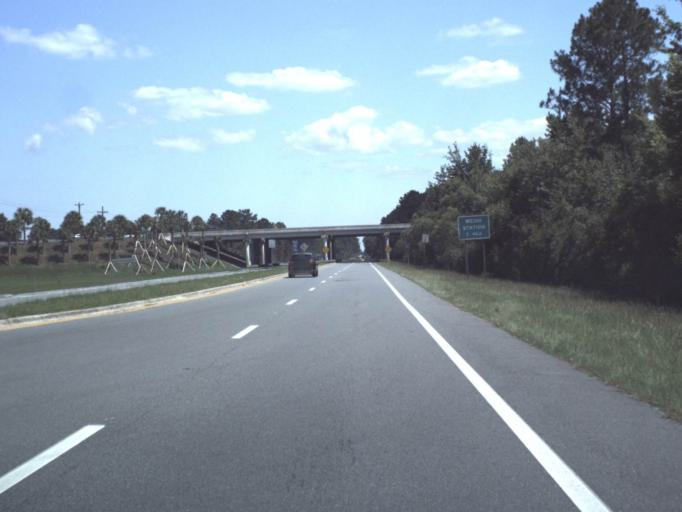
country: US
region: Georgia
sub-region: Camden County
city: Kingsland
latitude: 30.7131
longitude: -81.6730
